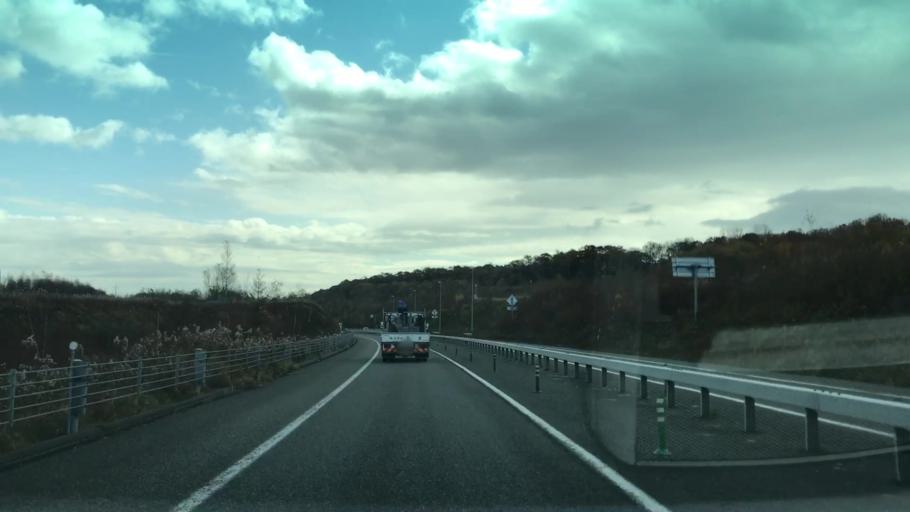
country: JP
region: Hokkaido
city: Tomakomai
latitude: 42.5460
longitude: 141.9977
